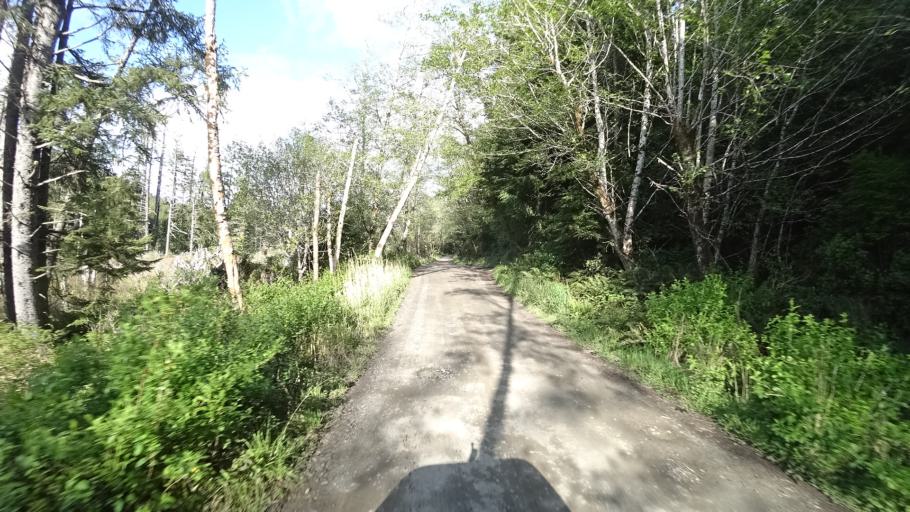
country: US
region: Oregon
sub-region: Douglas County
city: Reedsport
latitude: 43.7493
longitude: -124.1577
